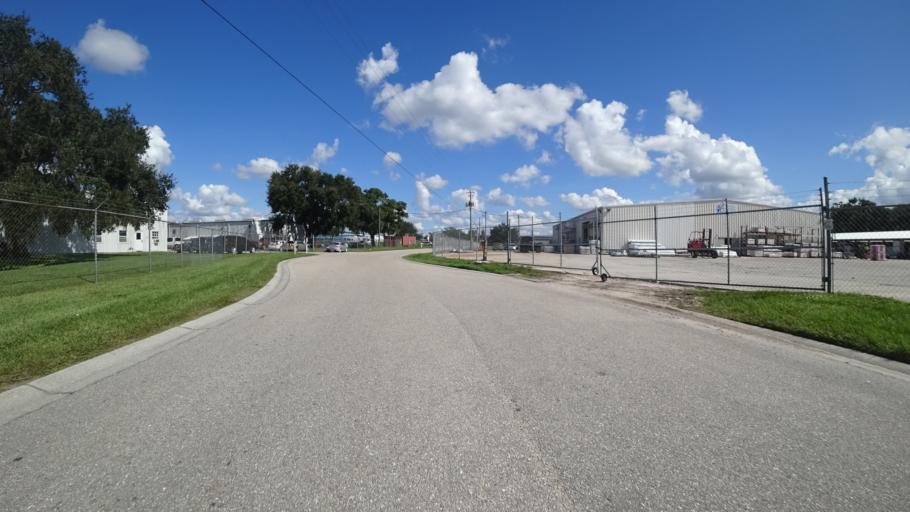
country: US
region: Florida
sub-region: Manatee County
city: Memphis
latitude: 27.5237
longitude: -82.5494
